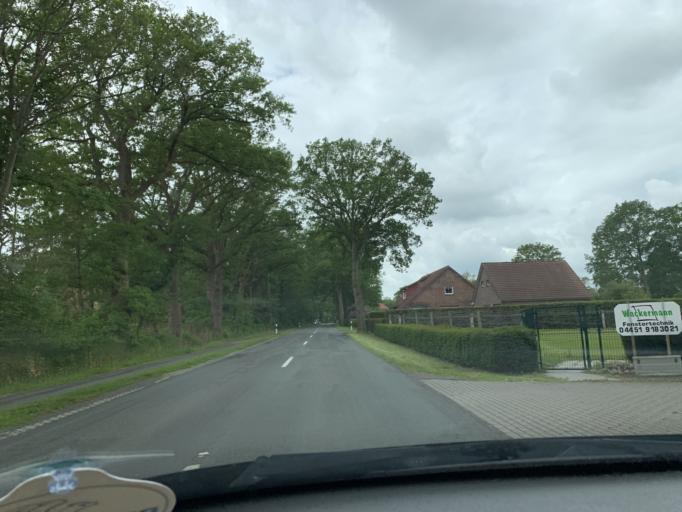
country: DE
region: Lower Saxony
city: Bockhorn
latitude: 53.3537
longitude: 8.0595
